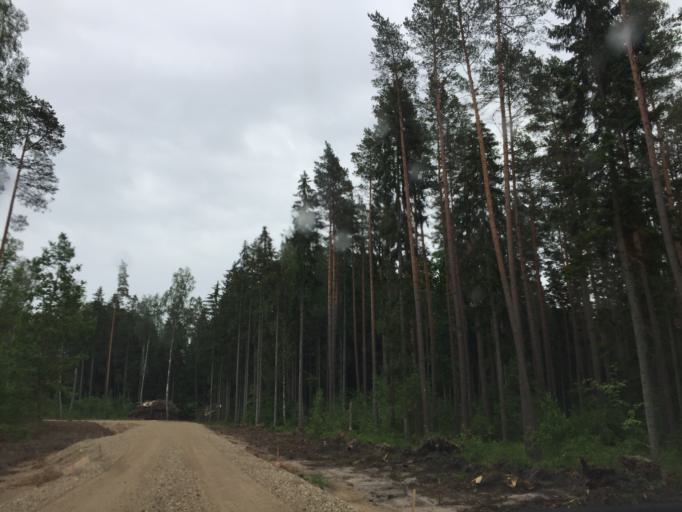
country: LV
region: Tukuma Rajons
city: Tukums
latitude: 57.0037
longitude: 23.1098
